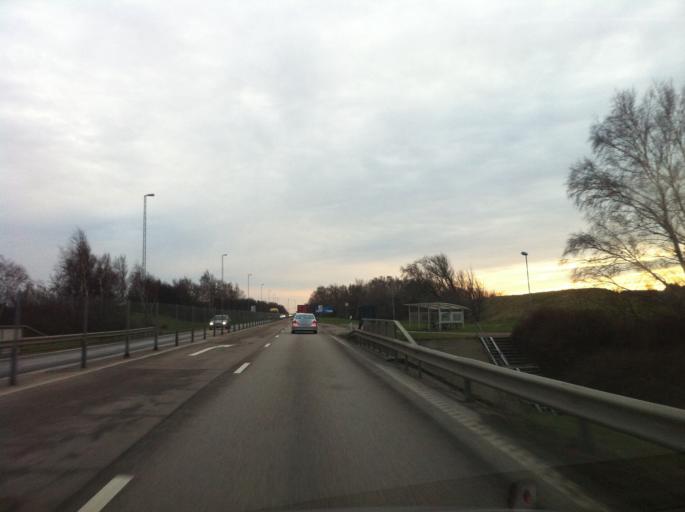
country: SE
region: Skane
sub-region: Hoganas Kommun
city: Hoganas
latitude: 56.1781
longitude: 12.5629
